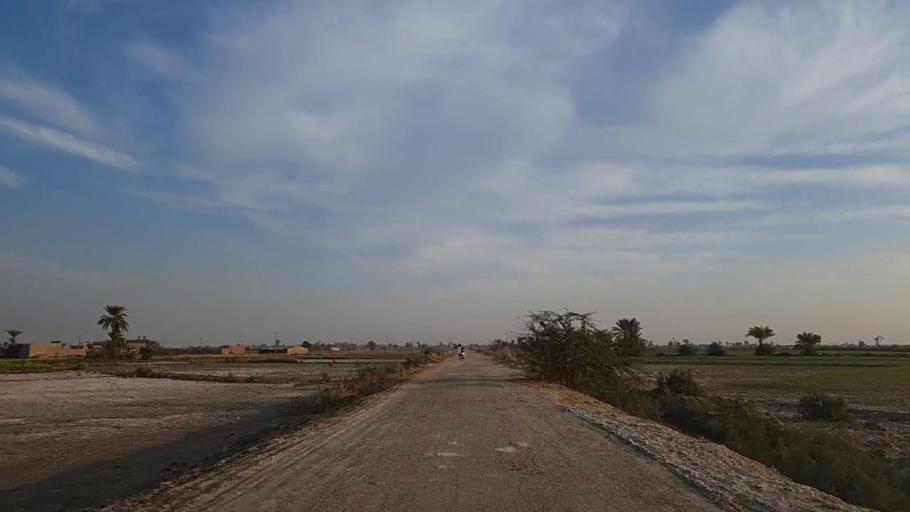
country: PK
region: Sindh
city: Bandhi
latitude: 26.5783
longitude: 68.3340
